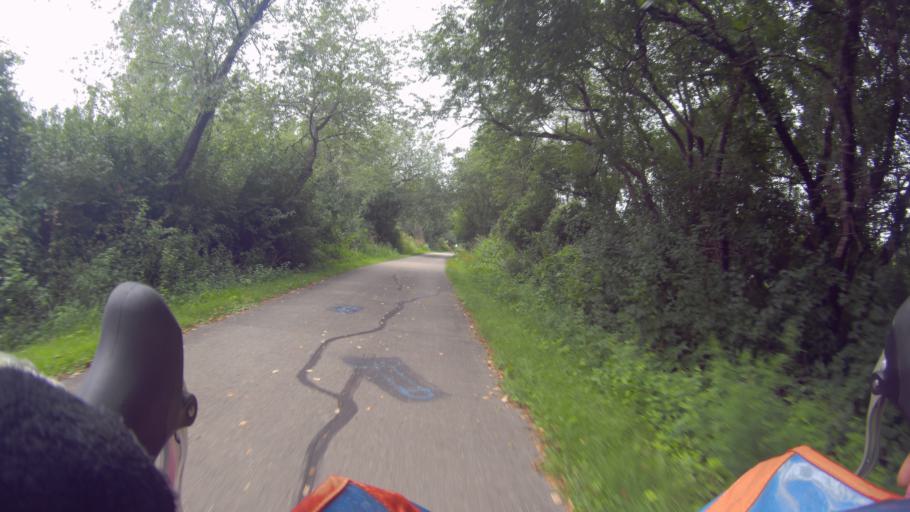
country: US
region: Wisconsin
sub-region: Dane County
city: Fitchburg
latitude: 43.0088
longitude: -89.4765
